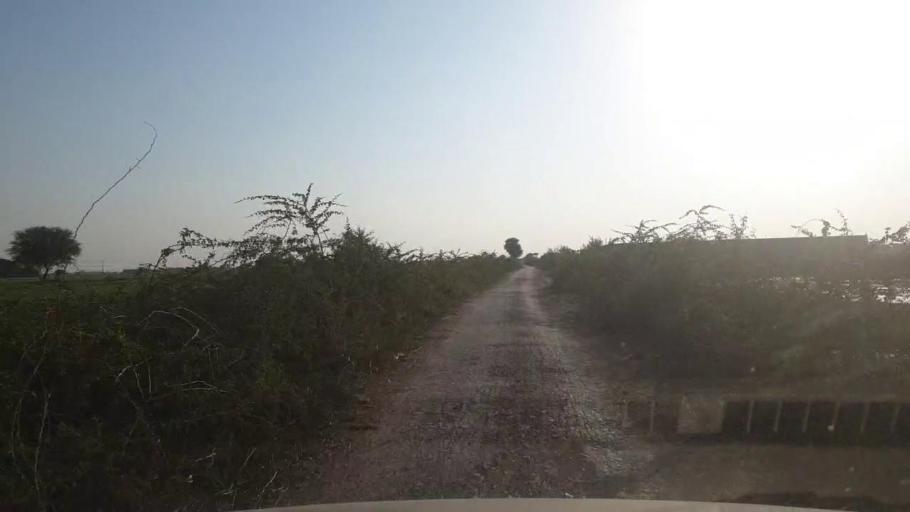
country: PK
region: Sindh
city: Chambar
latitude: 25.2563
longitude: 68.8854
